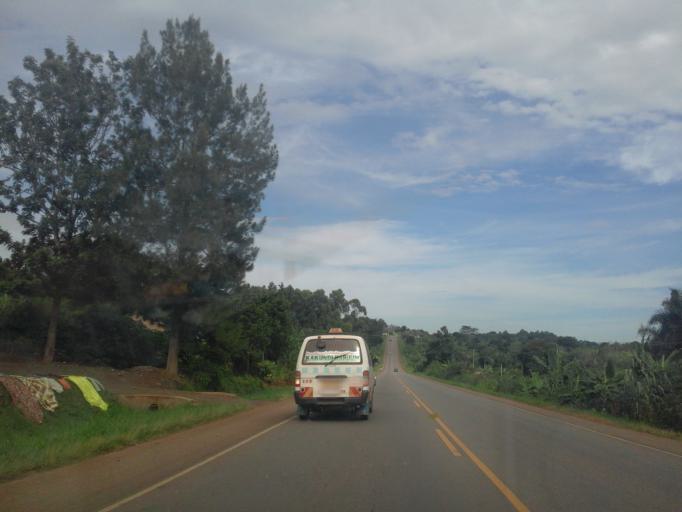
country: UG
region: Central Region
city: Masaka
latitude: -0.3472
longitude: 31.6122
